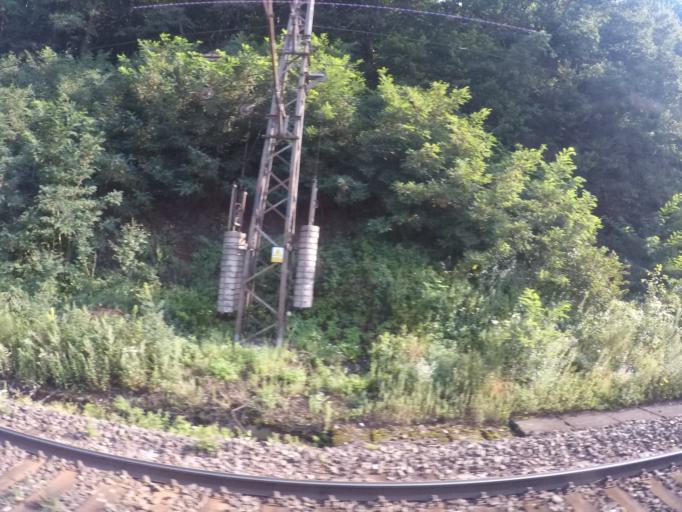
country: SK
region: Kosicky
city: Gelnica
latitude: 48.8931
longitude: 21.0297
